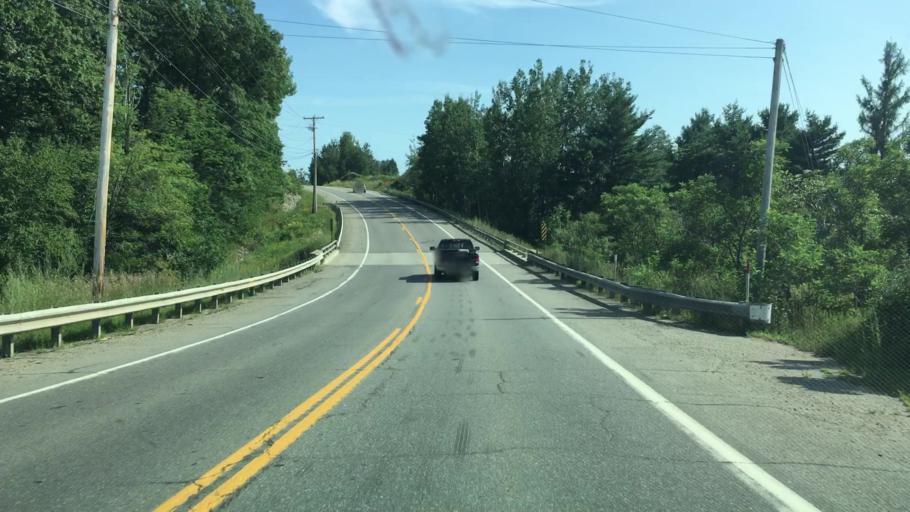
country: US
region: Maine
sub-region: Waldo County
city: Frankfort
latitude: 44.5587
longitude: -68.8661
